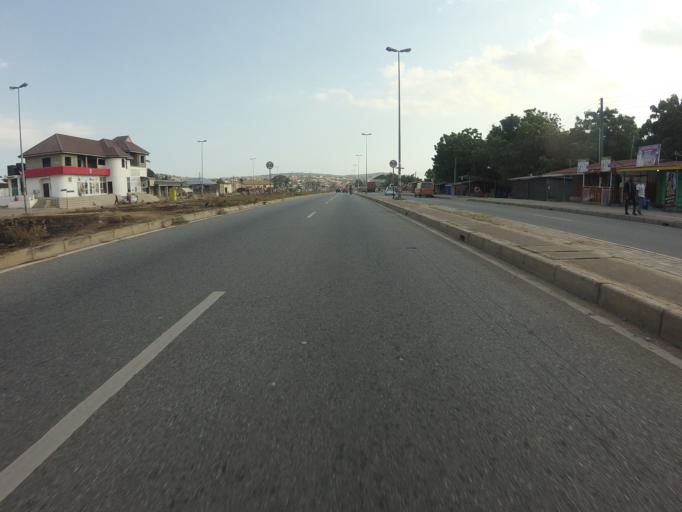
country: GH
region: Greater Accra
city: Gbawe
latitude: 5.6318
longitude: -0.3114
